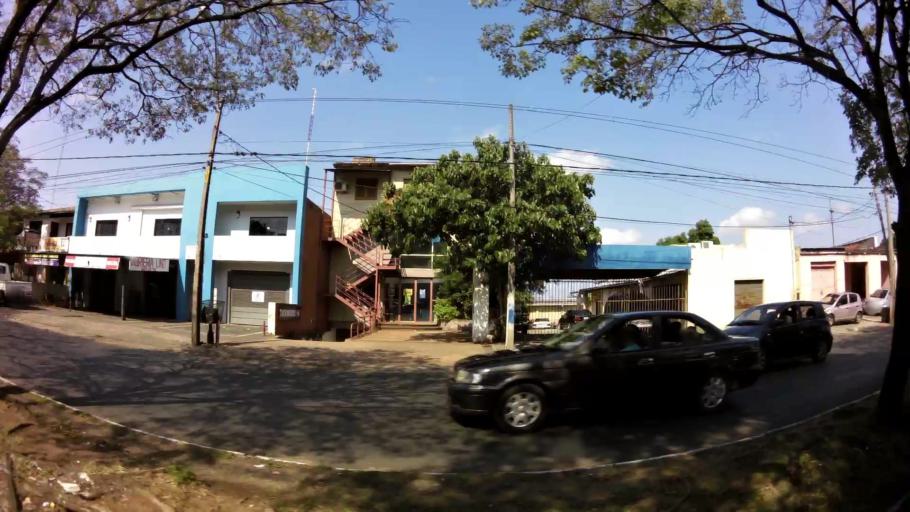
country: PY
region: Asuncion
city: Asuncion
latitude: -25.3078
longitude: -57.6318
